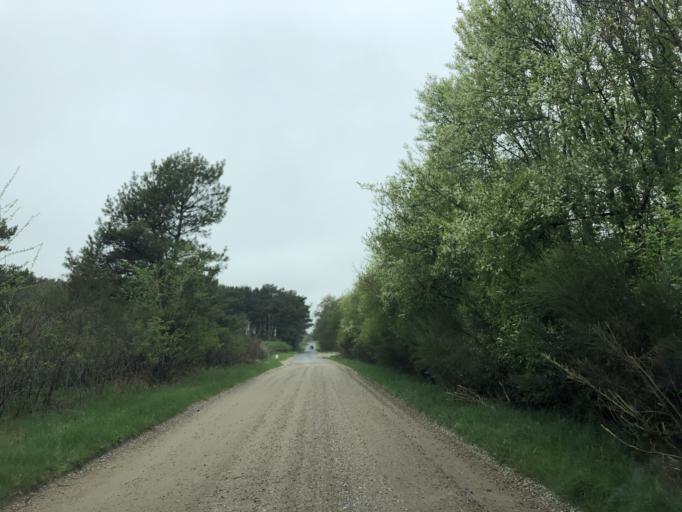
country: DK
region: Central Jutland
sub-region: Lemvig Kommune
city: Lemvig
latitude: 56.5106
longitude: 8.3164
